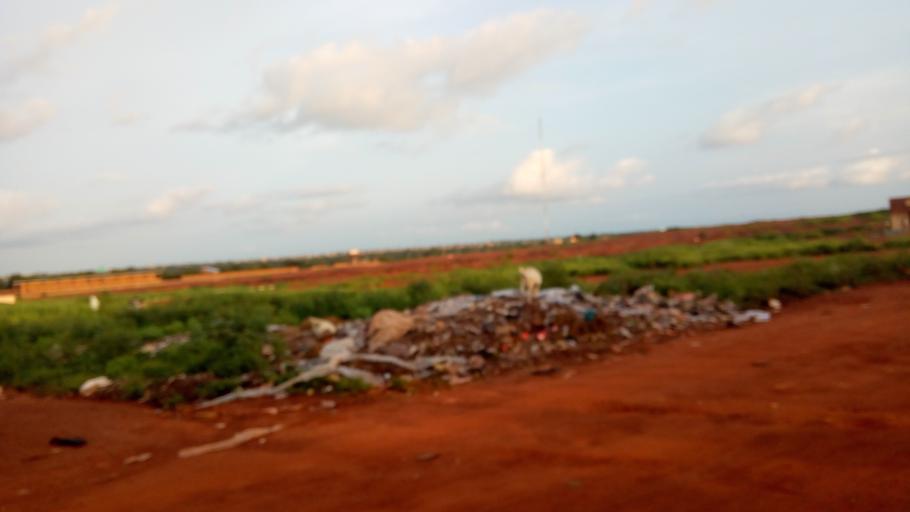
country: ML
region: Sikasso
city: Koutiala
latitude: 12.3751
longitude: -5.4801
